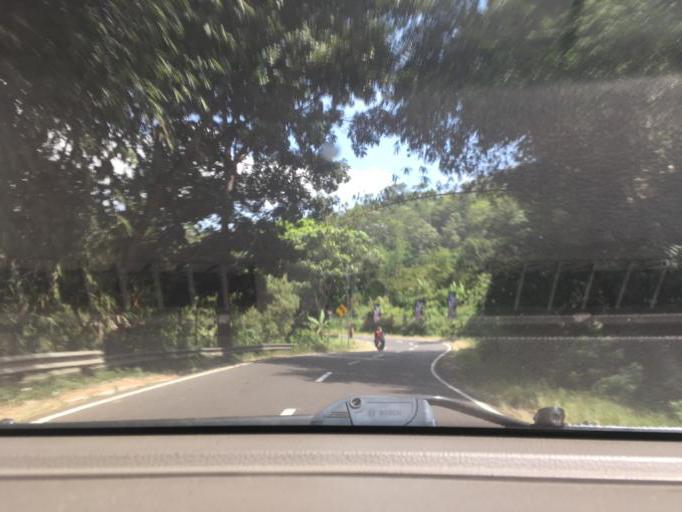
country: ID
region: West Java
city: Wage Cibahayu
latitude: -7.1165
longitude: 108.1159
